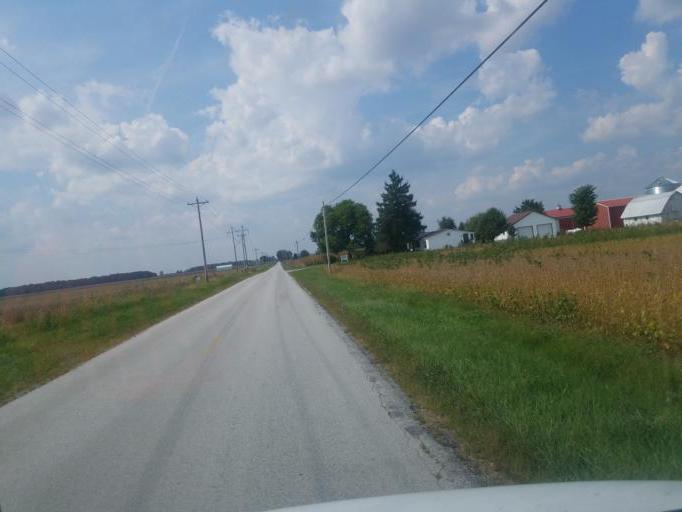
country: US
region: Ohio
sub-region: Hardin County
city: Kenton
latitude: 40.6432
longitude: -83.7266
